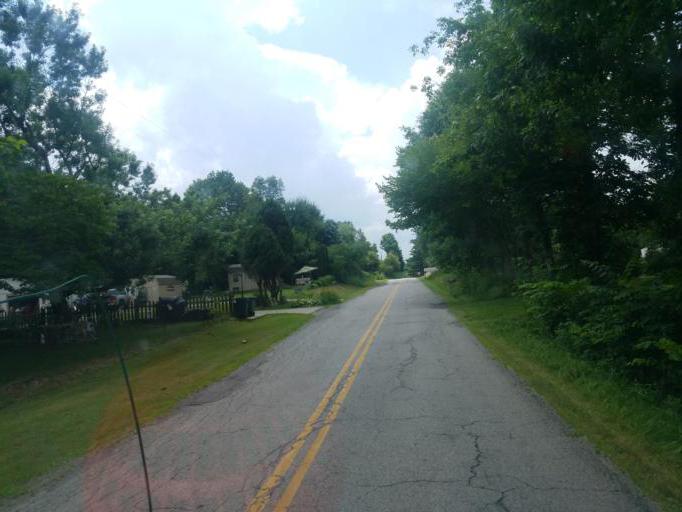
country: US
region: Ohio
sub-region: Mahoning County
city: Canfield
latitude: 40.9730
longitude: -80.8131
